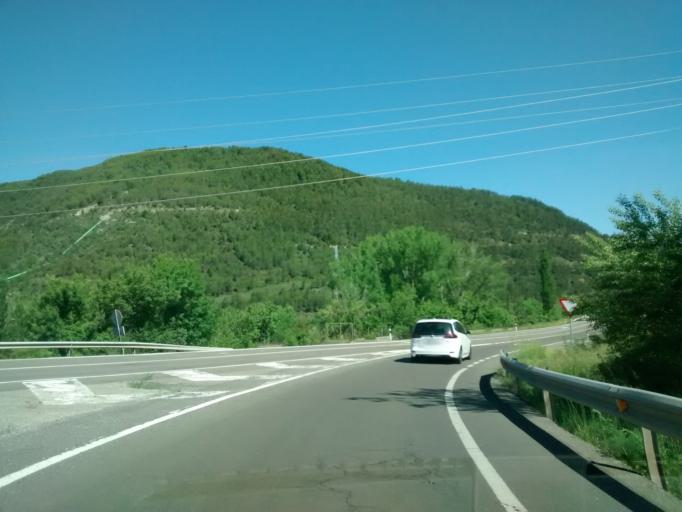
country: ES
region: Aragon
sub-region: Provincia de Huesca
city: Jaca
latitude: 42.5843
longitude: -0.5435
